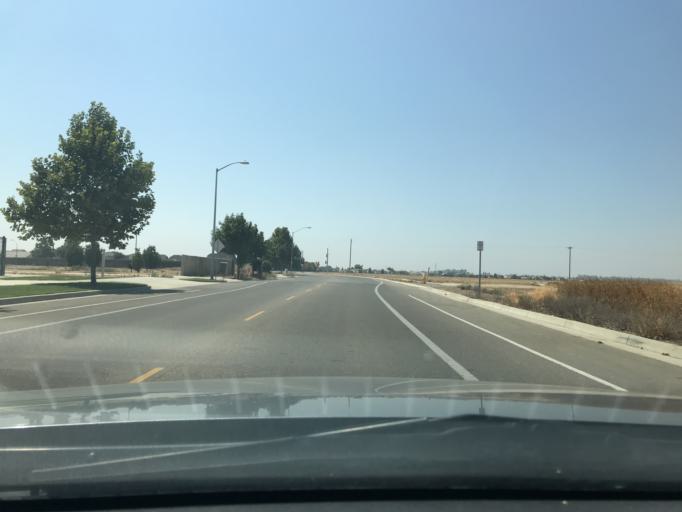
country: US
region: California
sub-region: Merced County
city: Merced
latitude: 37.3633
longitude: -120.4733
